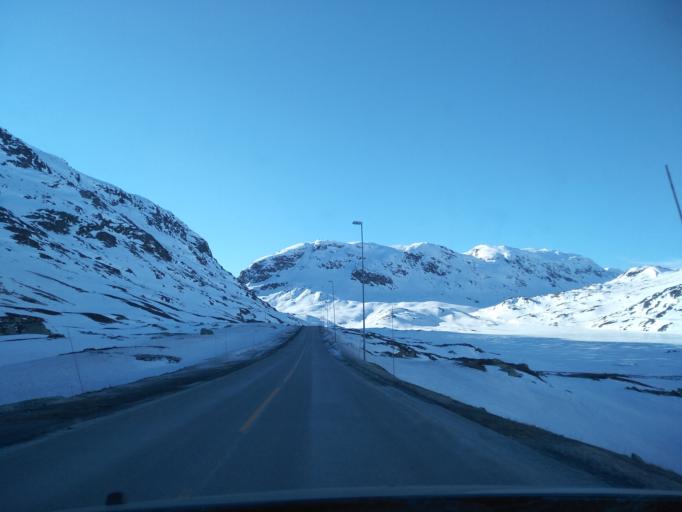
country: NO
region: Aust-Agder
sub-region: Bykle
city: Hovden
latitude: 59.8508
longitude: 7.0972
